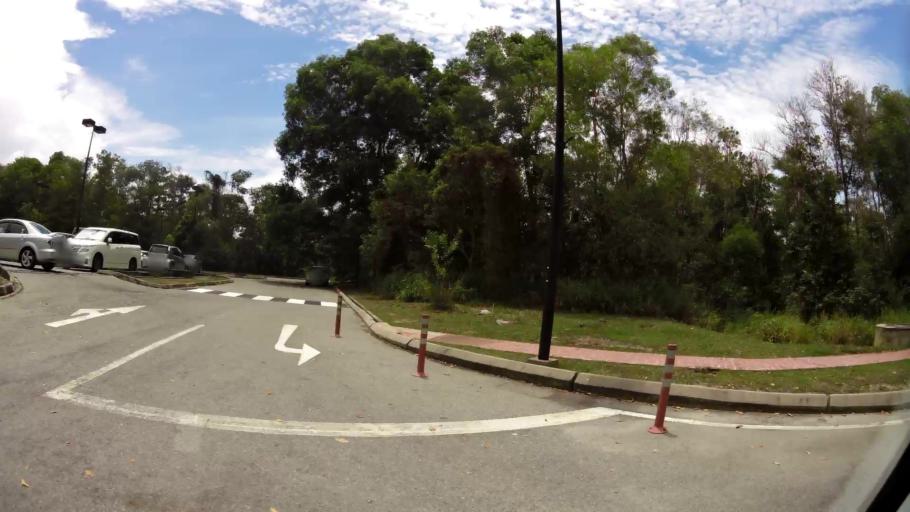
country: BN
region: Brunei and Muara
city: Bandar Seri Begawan
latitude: 4.9785
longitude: 114.9001
